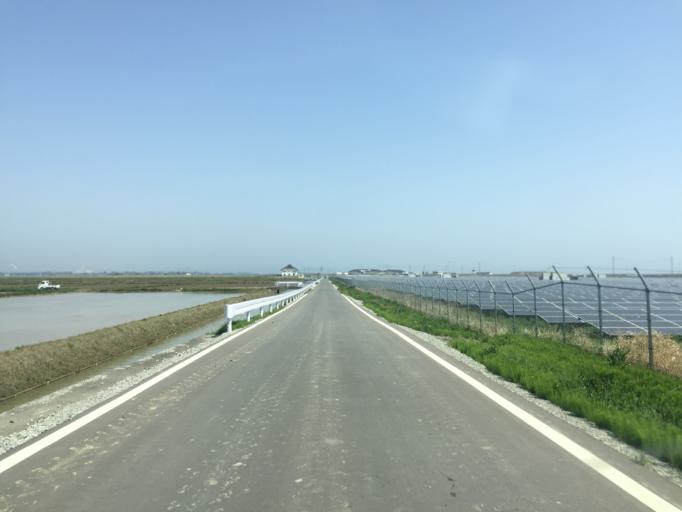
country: JP
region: Miyagi
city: Marumori
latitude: 37.7687
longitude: 140.9772
